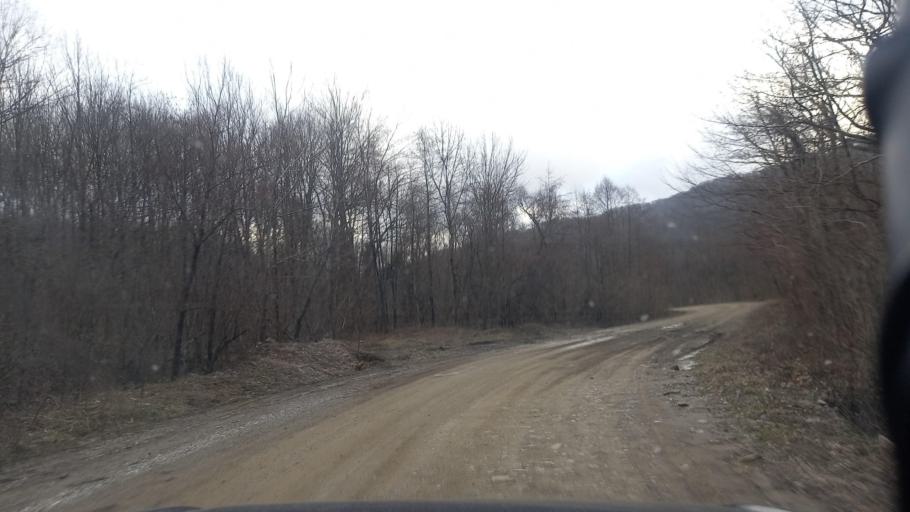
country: RU
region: Krasnodarskiy
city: Dzhubga
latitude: 44.4840
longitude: 38.7893
